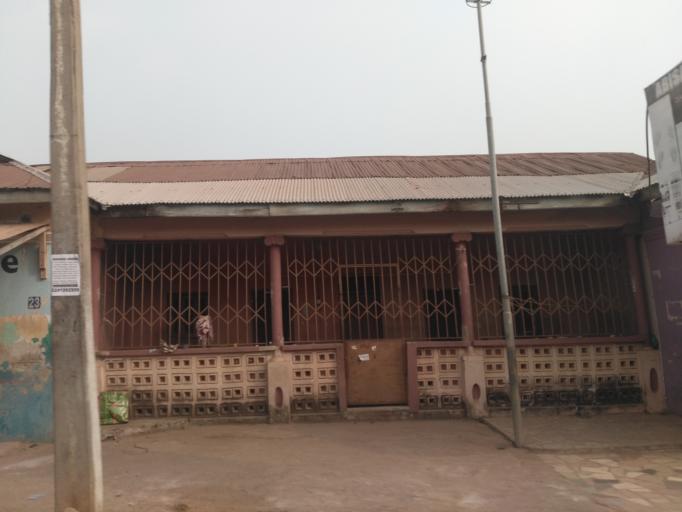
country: GH
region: Ashanti
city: Kumasi
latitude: 6.6949
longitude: -1.6108
